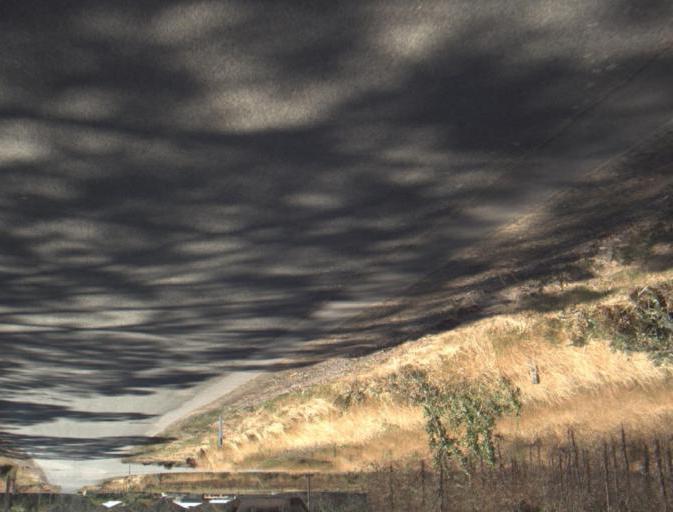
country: AU
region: Tasmania
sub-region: Launceston
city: Newstead
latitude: -41.3805
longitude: 147.2972
